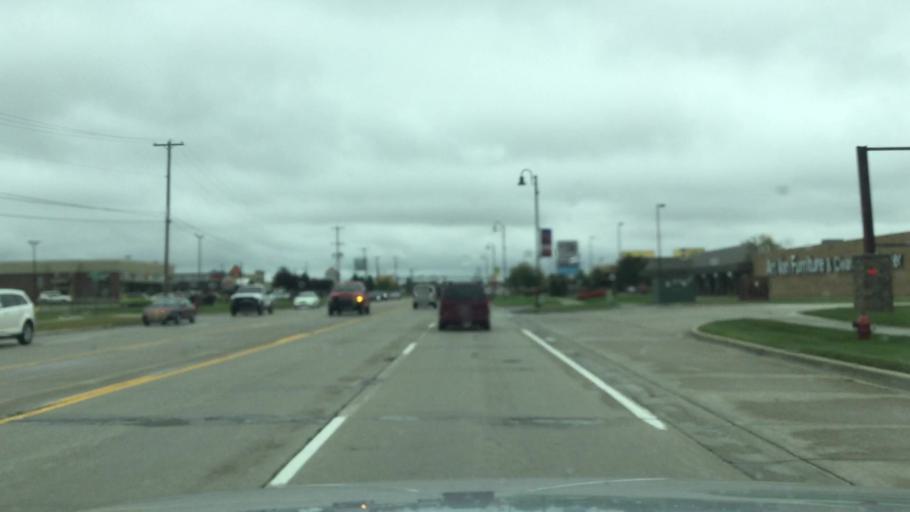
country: US
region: Michigan
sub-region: Saginaw County
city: Carrollton
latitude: 43.4801
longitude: -83.9668
